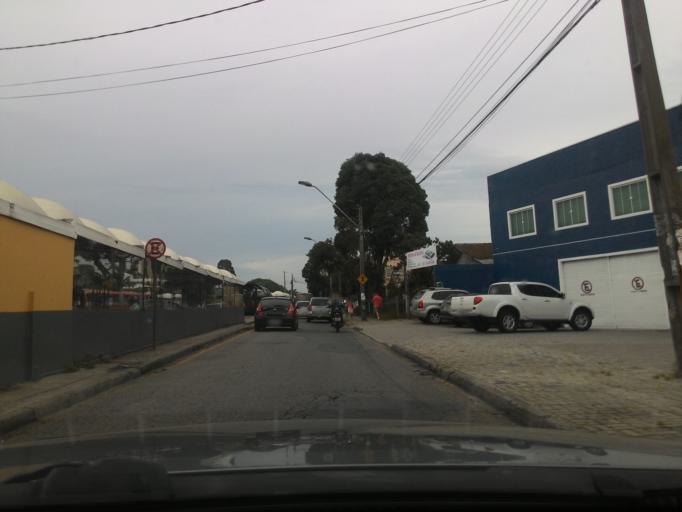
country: BR
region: Parana
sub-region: Pinhais
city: Pinhais
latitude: -25.4402
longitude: -49.2208
